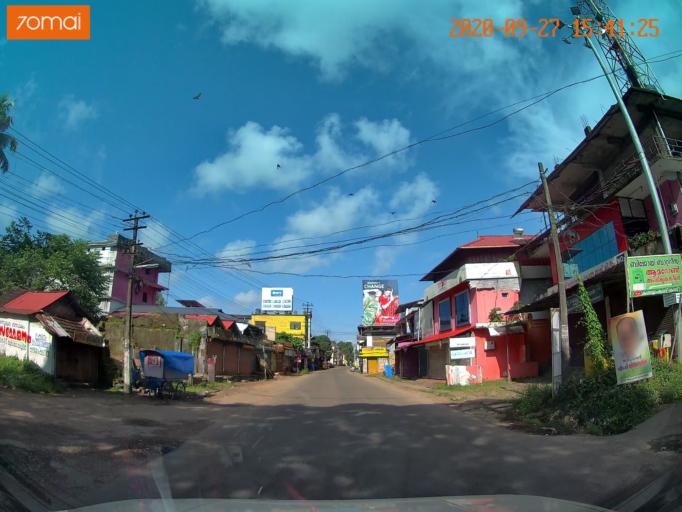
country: IN
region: Kerala
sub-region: Thrissur District
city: Thanniyam
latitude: 10.4711
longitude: 76.0949
